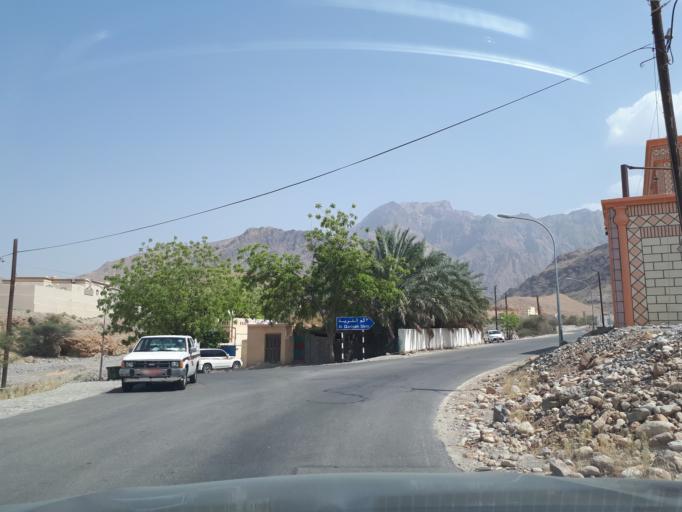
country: OM
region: Ash Sharqiyah
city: Ibra'
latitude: 23.0823
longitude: 58.8662
